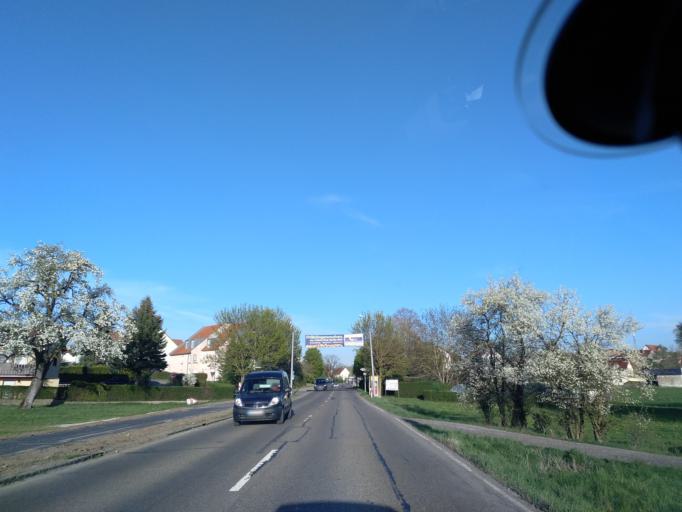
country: DE
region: Baden-Wuerttemberg
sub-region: Regierungsbezirk Stuttgart
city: Crailsheim
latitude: 49.1389
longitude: 10.0185
